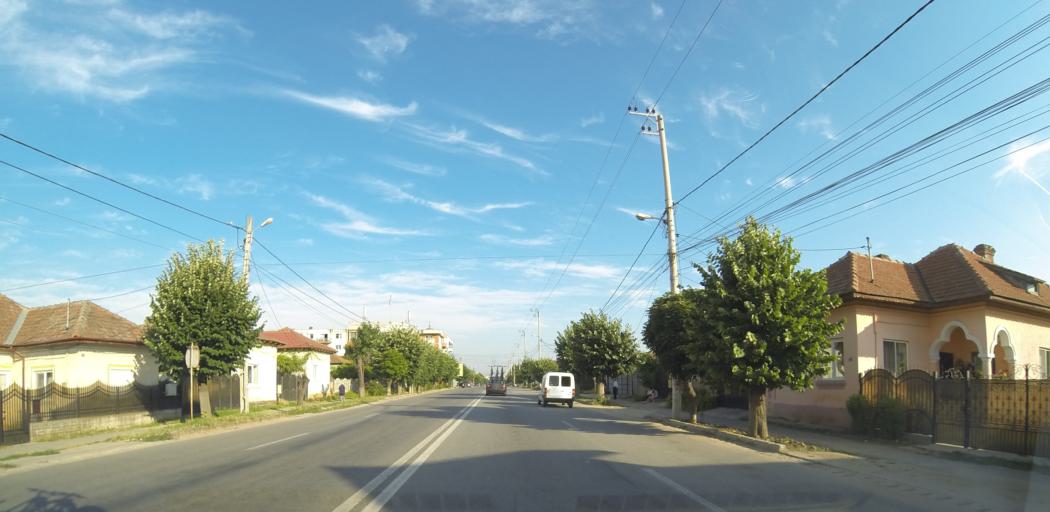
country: RO
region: Dolj
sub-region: Comuna Filiasi
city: Filiasi
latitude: 44.5512
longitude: 23.5263
